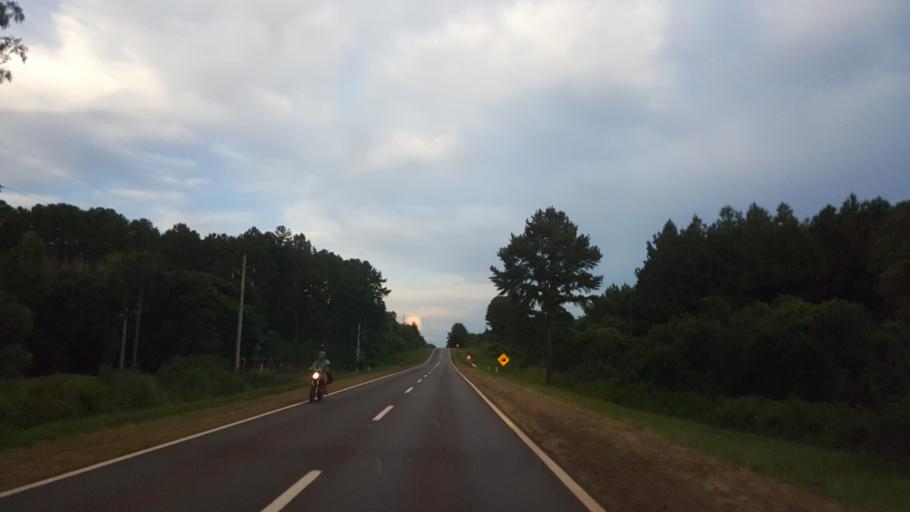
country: AR
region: Misiones
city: Jardin America
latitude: -27.0253
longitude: -55.2085
